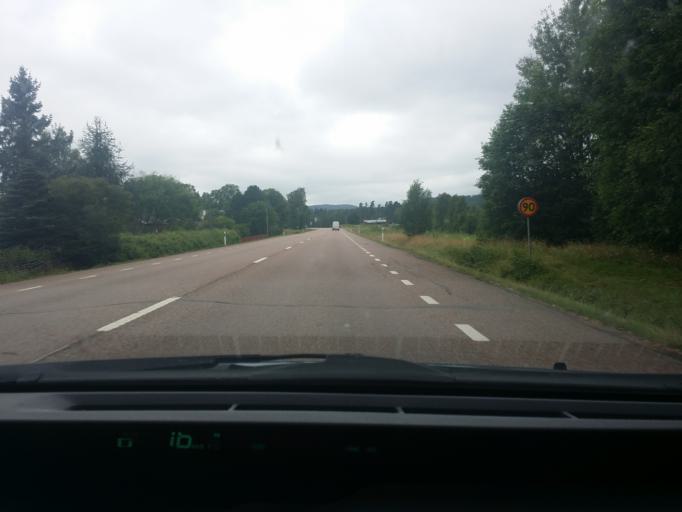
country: SE
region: Dalarna
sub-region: Gagnefs Kommun
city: Djuras
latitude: 60.5495
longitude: 15.2679
